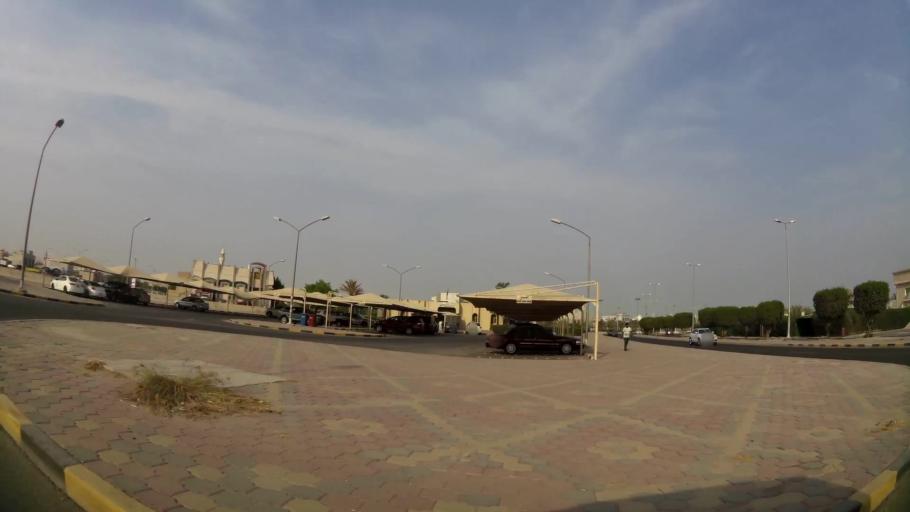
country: KW
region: Mubarak al Kabir
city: Sabah as Salim
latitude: 29.2540
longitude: 48.0531
